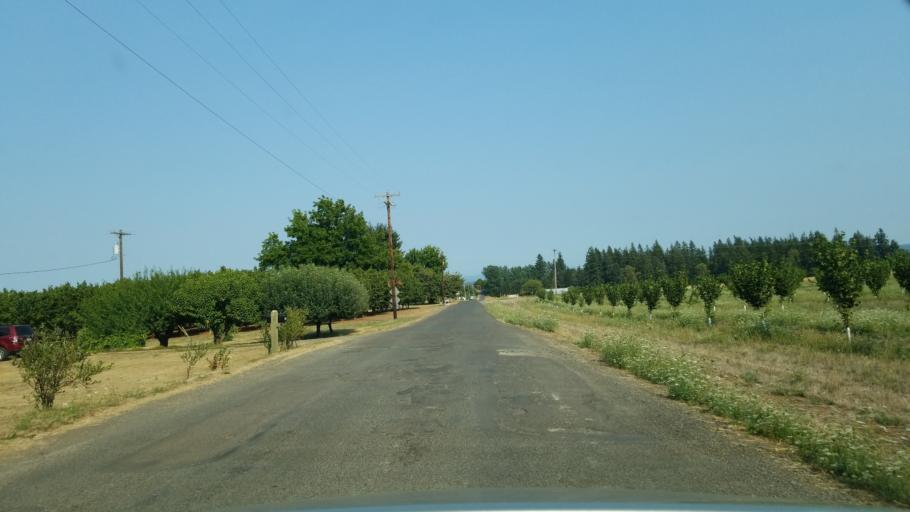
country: US
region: Oregon
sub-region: Marion County
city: Mount Angel
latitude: 45.0712
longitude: -122.7169
